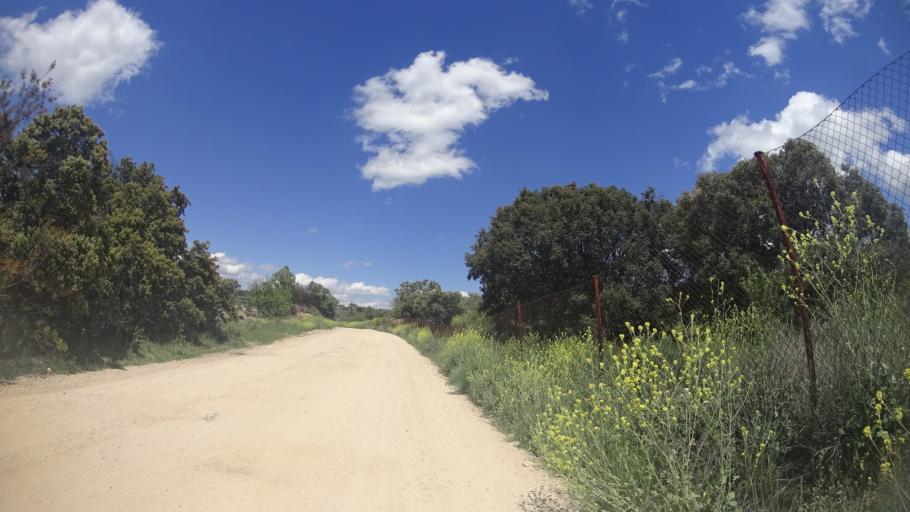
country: ES
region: Madrid
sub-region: Provincia de Madrid
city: San Martin de Valdeiglesias
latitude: 40.3644
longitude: -4.3859
